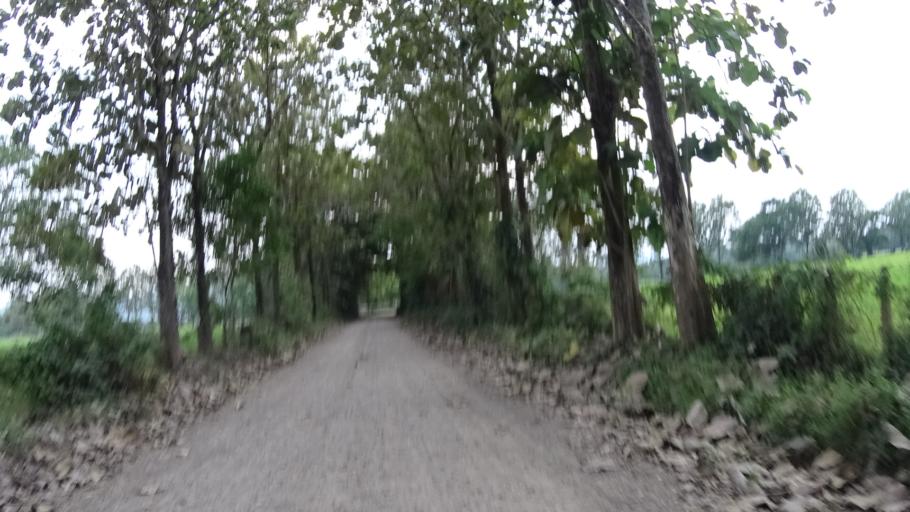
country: CO
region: Cundinamarca
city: Puerto Salgar
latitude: 5.4864
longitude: -74.6973
